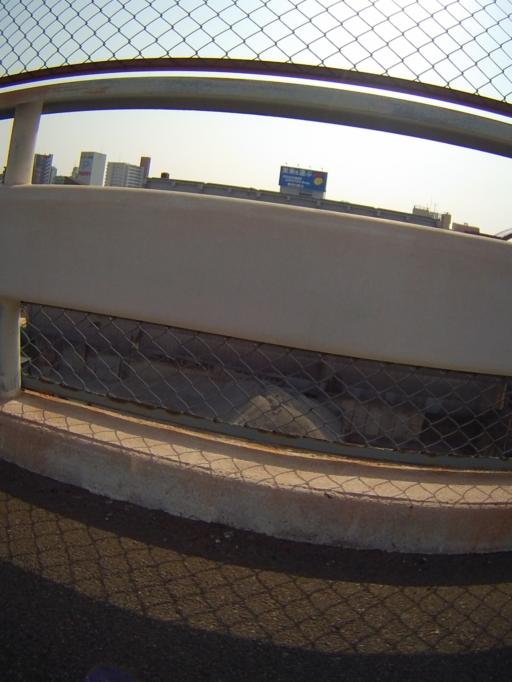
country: JP
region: Osaka
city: Osaka-shi
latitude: 34.6756
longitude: 135.4581
